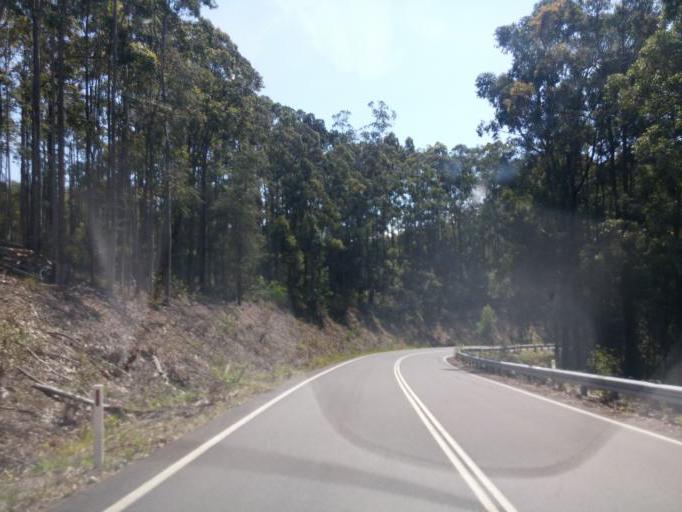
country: AU
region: New South Wales
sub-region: Great Lakes
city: Bulahdelah
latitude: -32.3899
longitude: 152.2472
